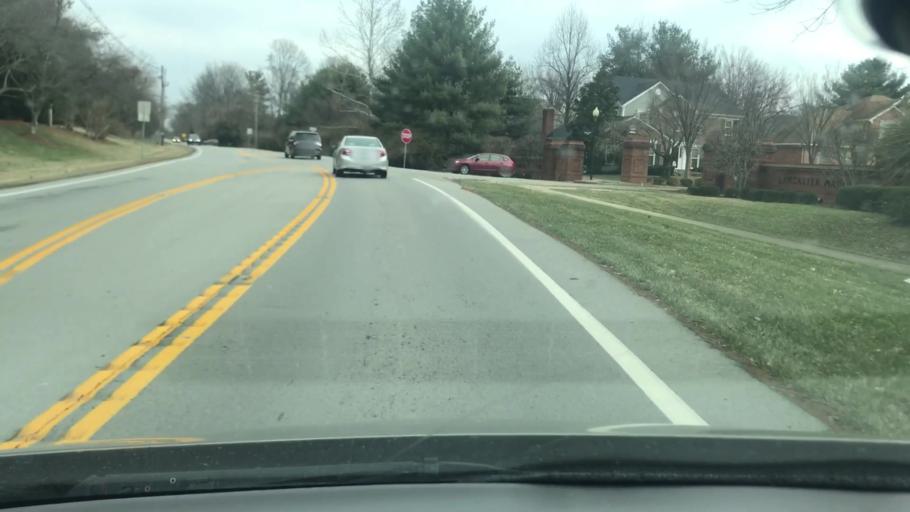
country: US
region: Kentucky
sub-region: Jefferson County
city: Graymoor-Devondale
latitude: 38.2886
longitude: -85.6197
